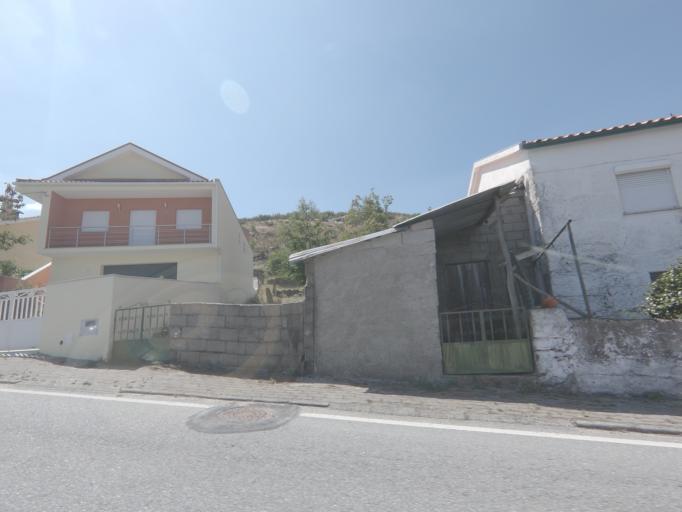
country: PT
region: Viseu
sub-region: Tarouca
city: Tarouca
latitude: 40.9870
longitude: -7.7821
